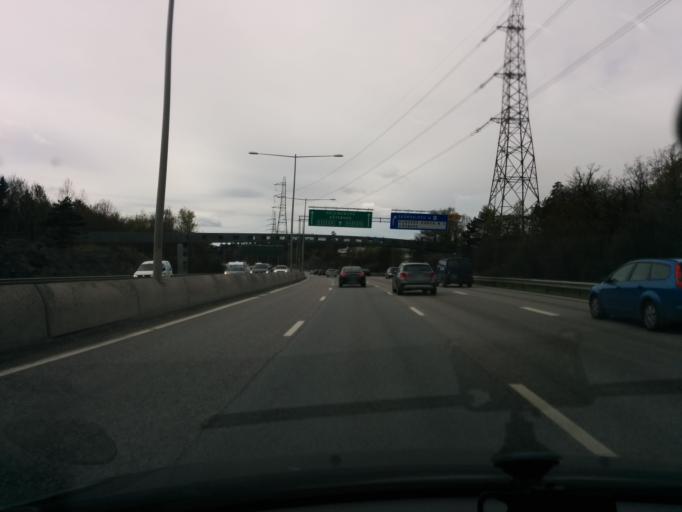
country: SE
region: Stockholm
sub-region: Huddinge Kommun
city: Segeltorp
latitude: 59.2827
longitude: 17.9272
